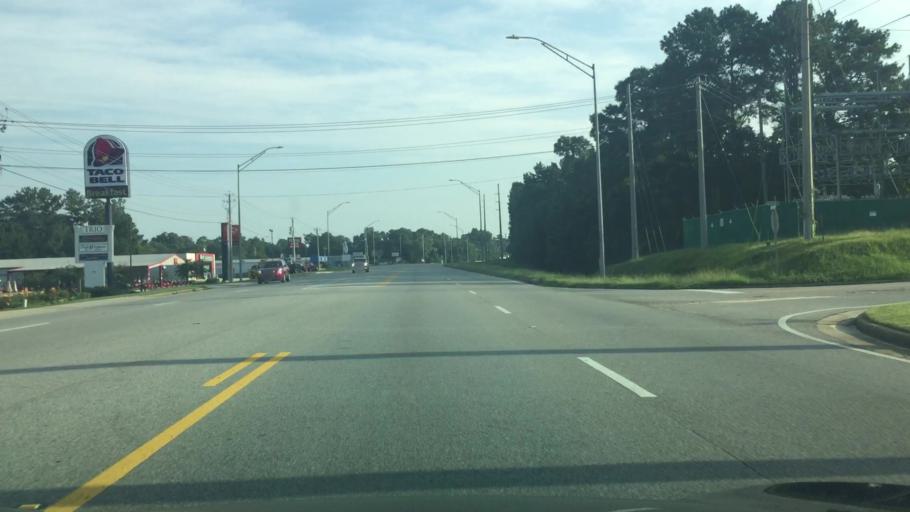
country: US
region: Alabama
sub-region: Covington County
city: Andalusia
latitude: 31.3101
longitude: -86.4994
